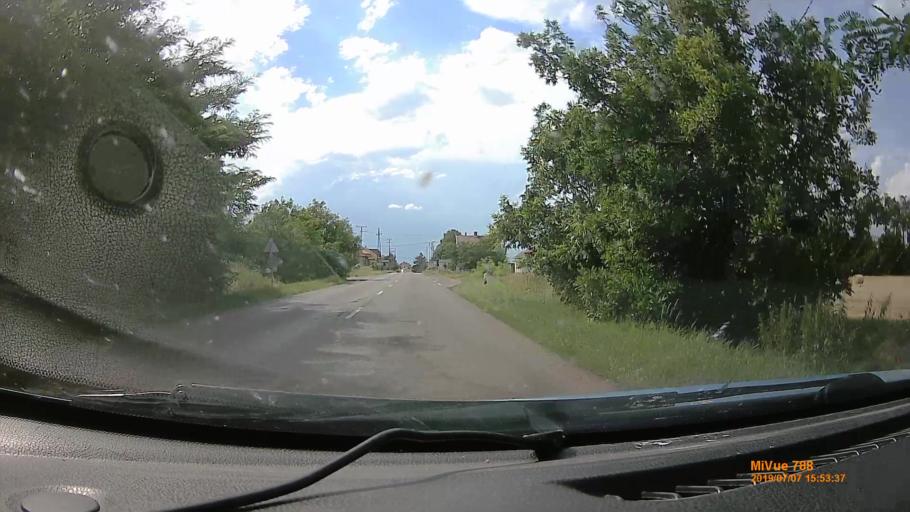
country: HU
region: Pest
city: Szentlorinckata
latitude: 47.5504
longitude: 19.8031
